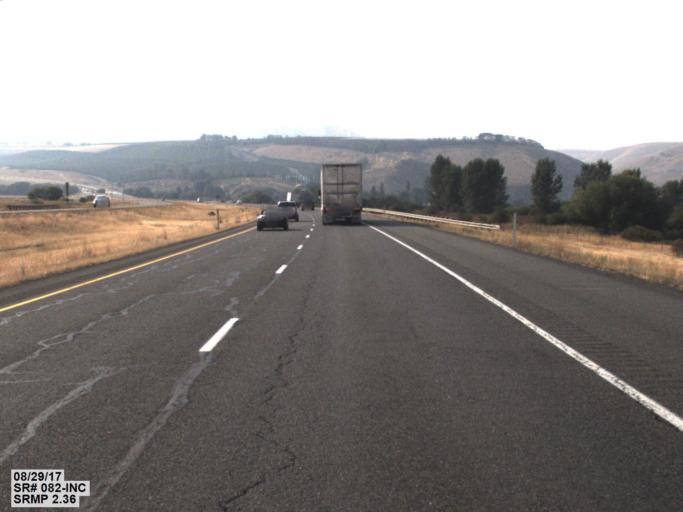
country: US
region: Washington
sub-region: Kittitas County
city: Ellensburg
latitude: 46.9374
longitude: -120.5070
